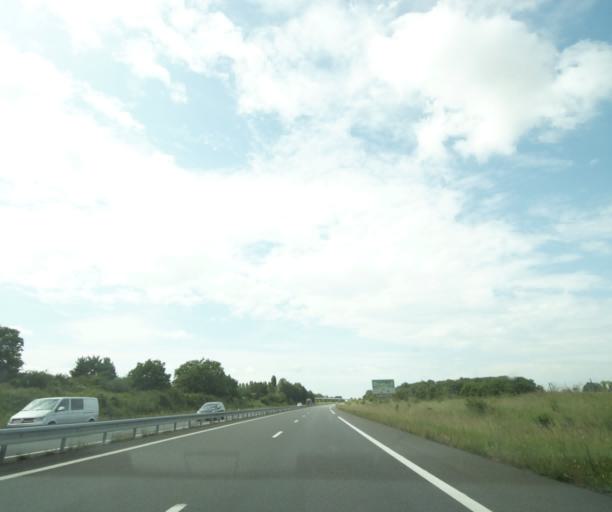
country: FR
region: Pays de la Loire
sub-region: Departement de Maine-et-Loire
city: Vivy
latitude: 47.3527
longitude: -0.0764
